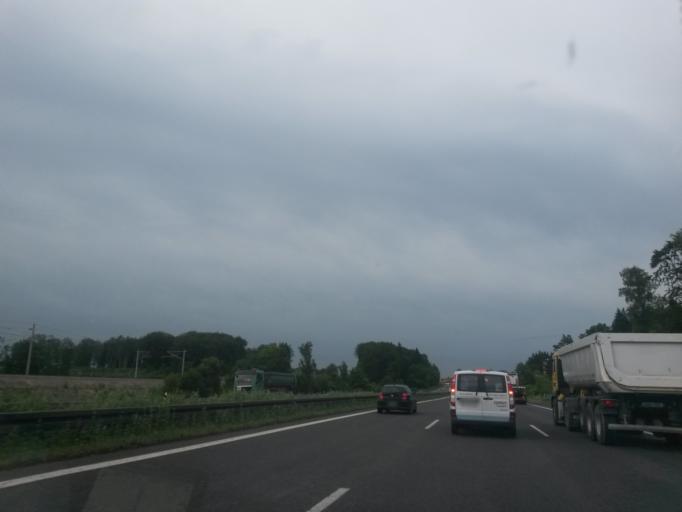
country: DE
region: Bavaria
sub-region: Upper Bavaria
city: Stammham
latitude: 48.8870
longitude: 11.4663
